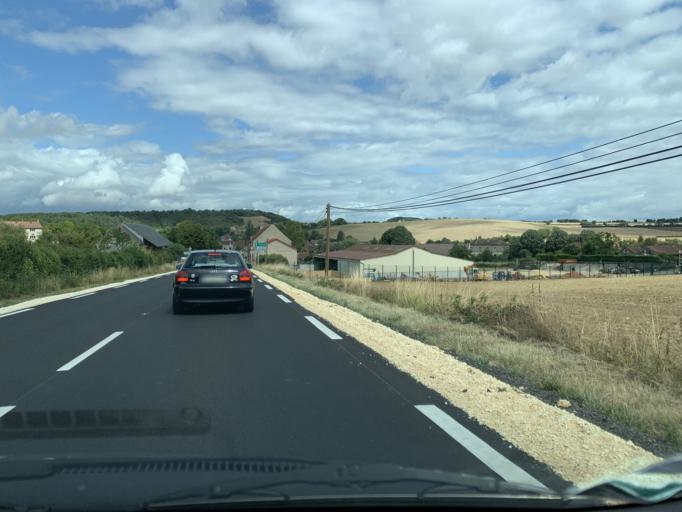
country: FR
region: Bourgogne
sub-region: Departement de la Nievre
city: Varzy
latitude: 47.3523
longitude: 3.3813
